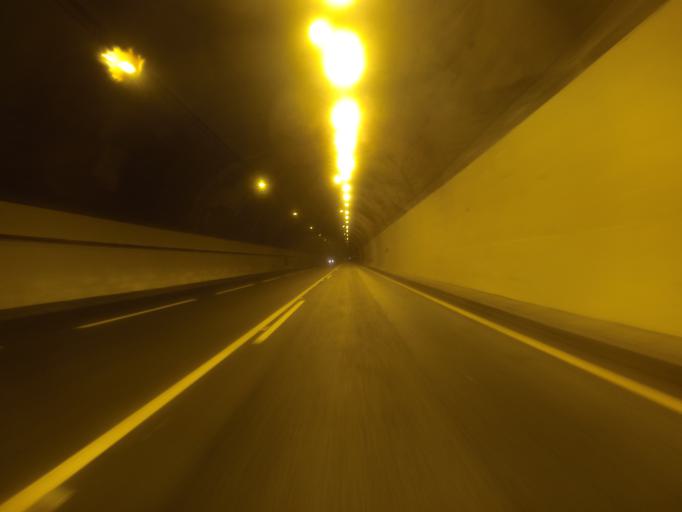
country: PT
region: Madeira
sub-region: Santa Cruz
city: Camacha
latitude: 32.6671
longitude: -16.8511
